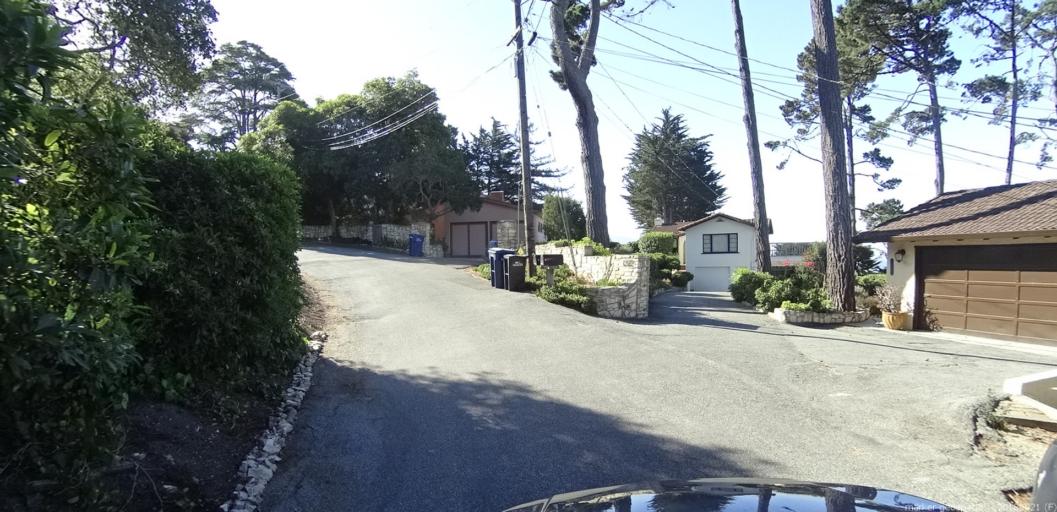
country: US
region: California
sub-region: Monterey County
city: Carmel-by-the-Sea
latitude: 36.5675
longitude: -121.9149
